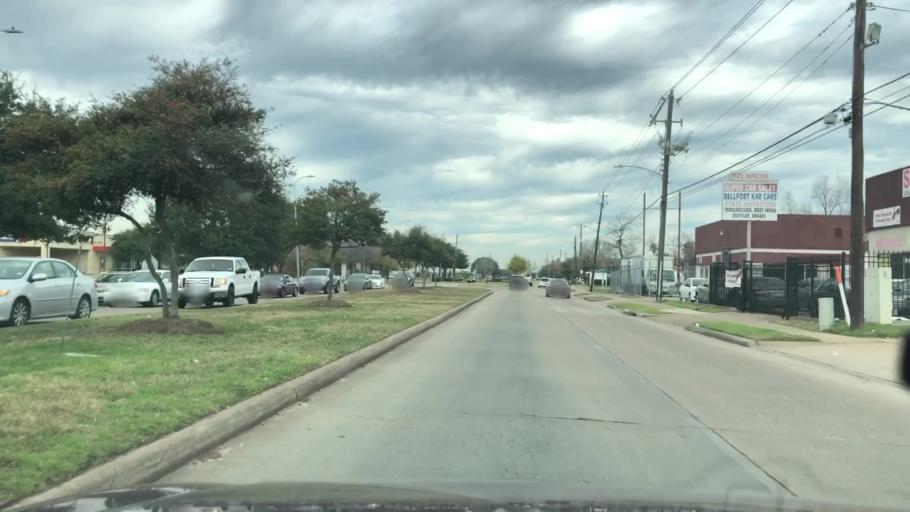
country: US
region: Texas
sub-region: Fort Bend County
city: Missouri City
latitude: 29.6560
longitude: -95.5280
